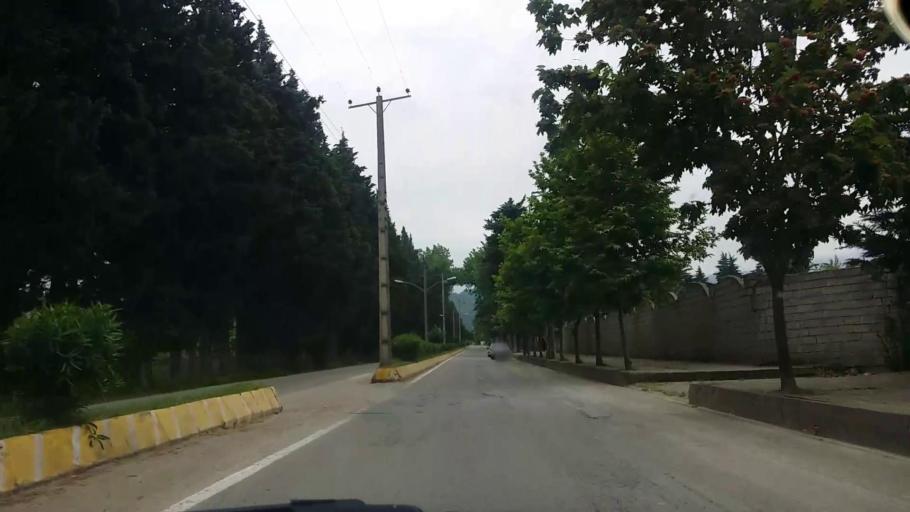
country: IR
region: Mazandaran
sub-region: Nowshahr
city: Nowshahr
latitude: 36.6336
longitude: 51.5026
